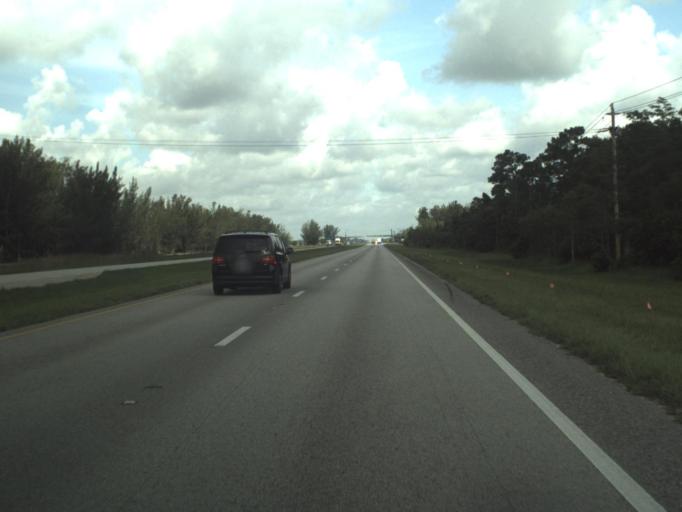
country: US
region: Florida
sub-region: Palm Beach County
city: Palm Beach Gardens
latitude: 26.8055
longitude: -80.1456
